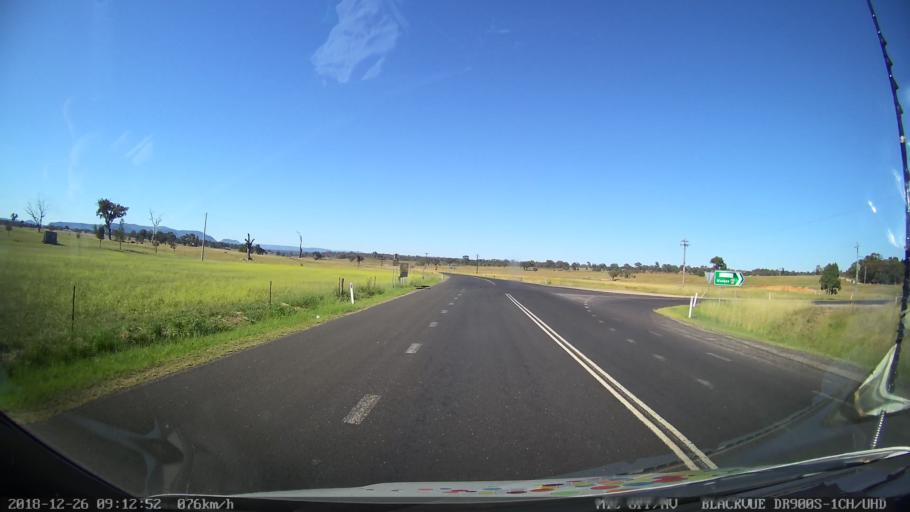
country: AU
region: New South Wales
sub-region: Mid-Western Regional
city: Kandos
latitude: -32.7619
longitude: 149.9790
